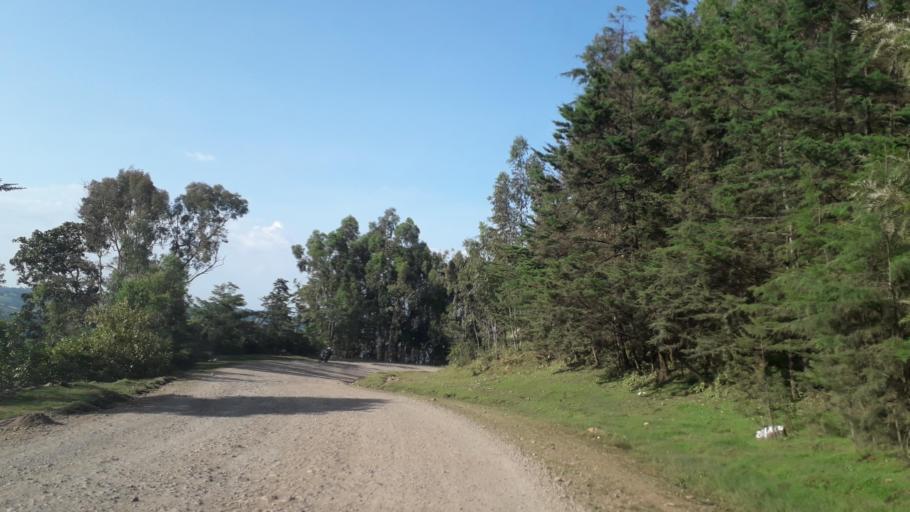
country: ET
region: Oromiya
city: Jima
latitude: 7.4639
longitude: 36.8707
